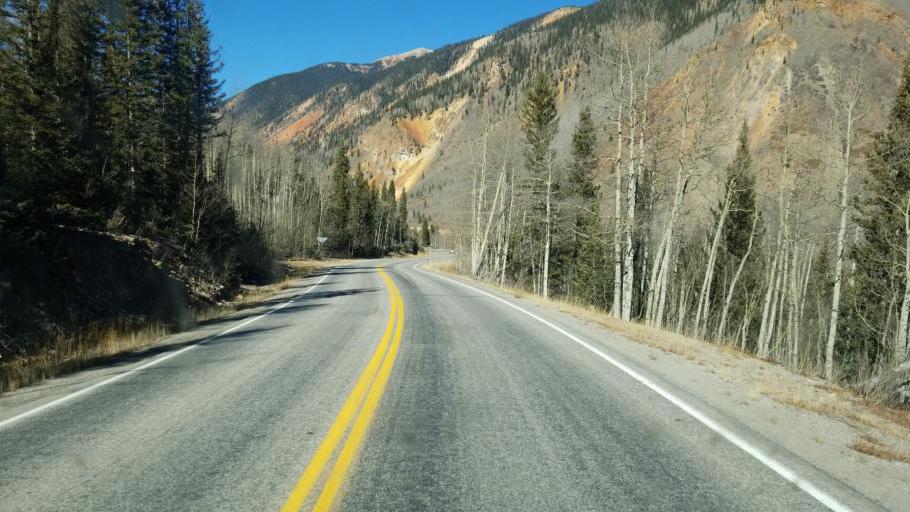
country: US
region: Colorado
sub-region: San Juan County
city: Silverton
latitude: 37.8031
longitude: -107.6779
